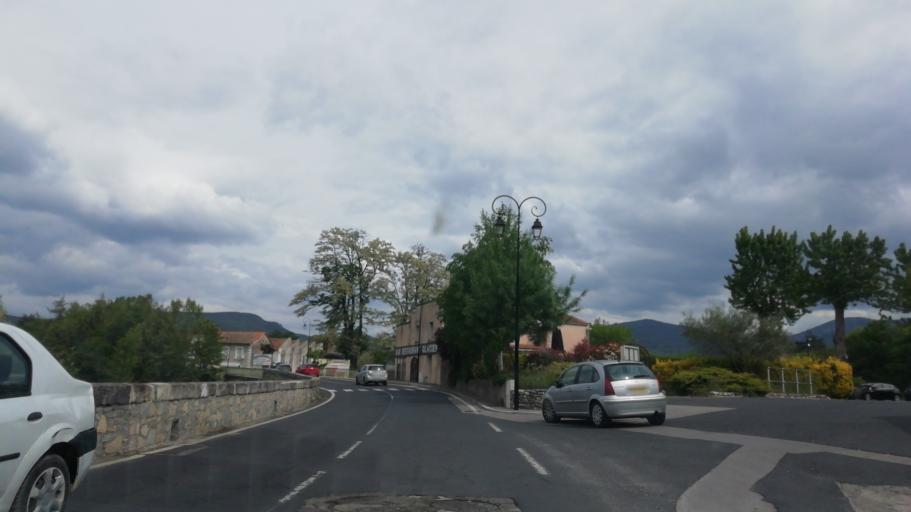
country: FR
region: Languedoc-Roussillon
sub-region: Departement de l'Herault
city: Laroque
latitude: 43.9228
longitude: 3.7228
